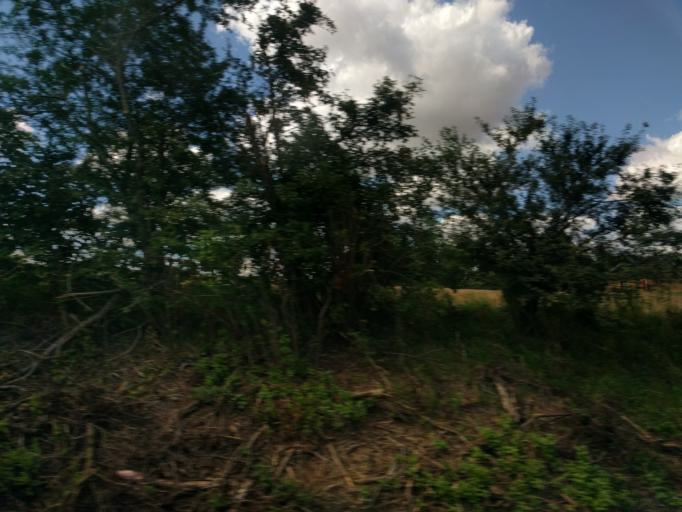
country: DK
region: Zealand
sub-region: Roskilde Kommune
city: Viby
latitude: 55.5739
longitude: 12.0355
